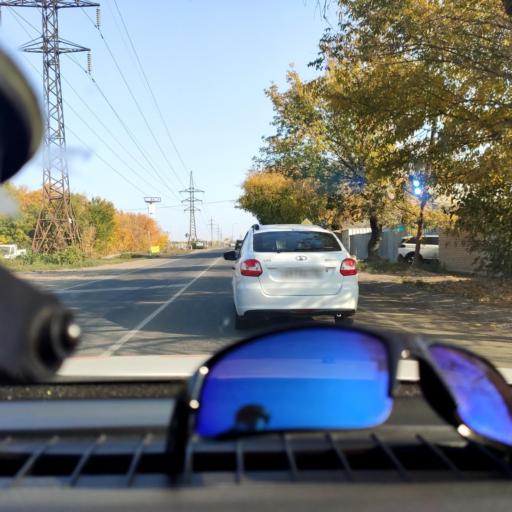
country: RU
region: Samara
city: Samara
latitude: 53.1325
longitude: 50.1341
